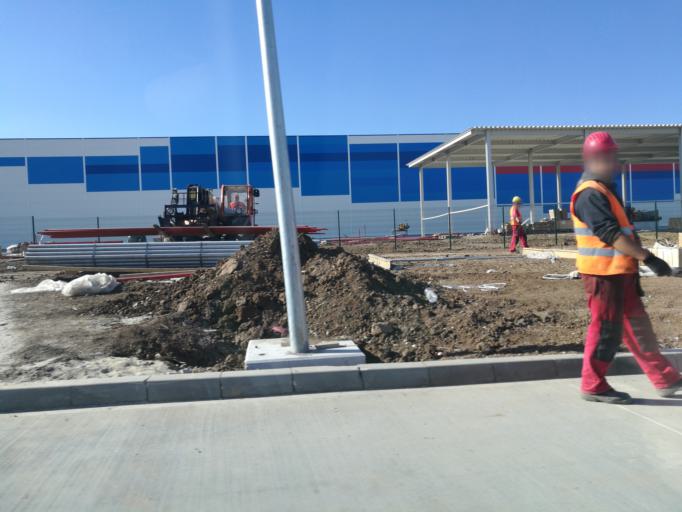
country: RO
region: Giurgiu
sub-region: Comuna Joita
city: Bacu
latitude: 44.4673
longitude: 25.8782
